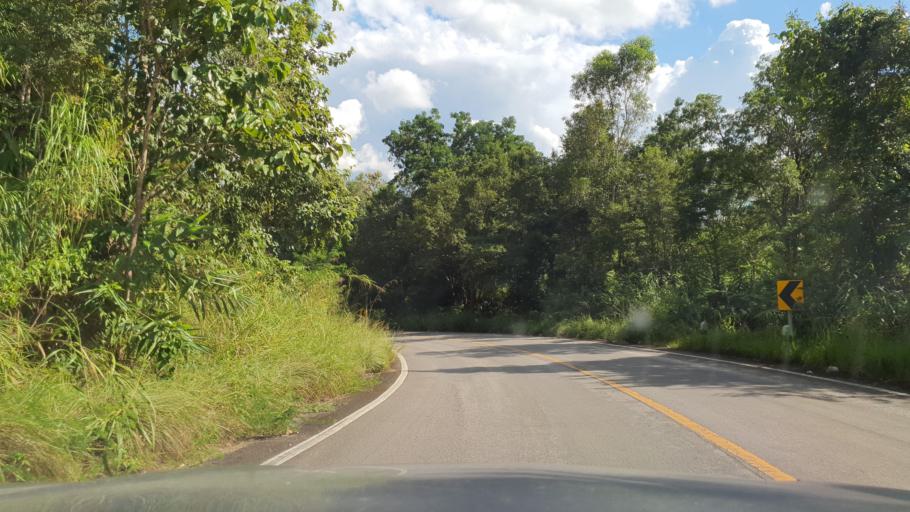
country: TH
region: Chiang Rai
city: Wiang Pa Pao
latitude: 19.3325
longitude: 99.4598
